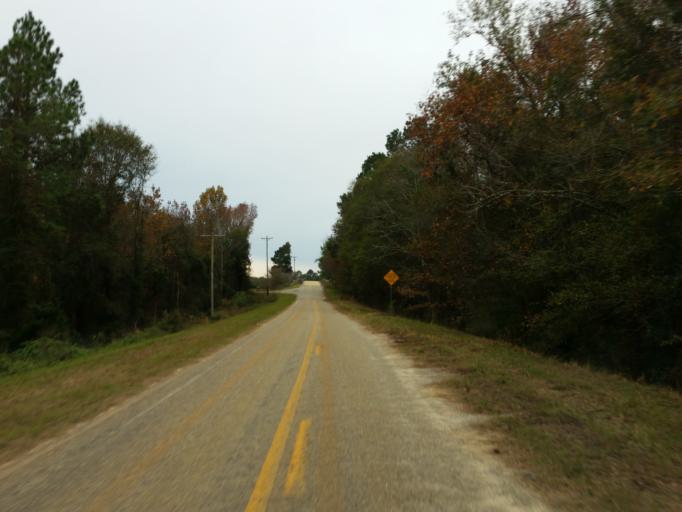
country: US
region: Georgia
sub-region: Crisp County
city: Cordele
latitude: 31.8771
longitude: -83.7245
